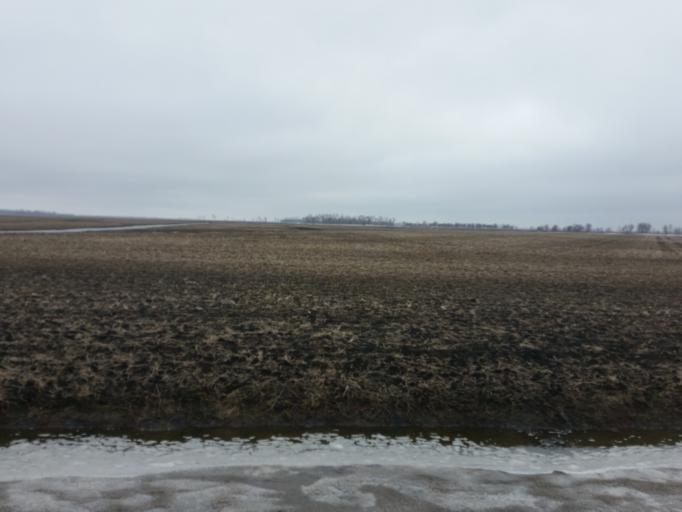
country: US
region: North Dakota
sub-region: Walsh County
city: Grafton
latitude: 48.3831
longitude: -97.2187
